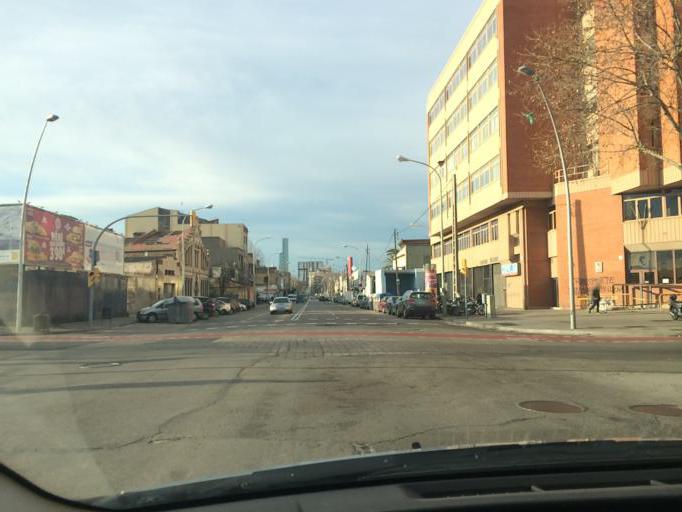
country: ES
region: Catalonia
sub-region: Provincia de Barcelona
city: Sant Marti
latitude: 41.4154
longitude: 2.2073
